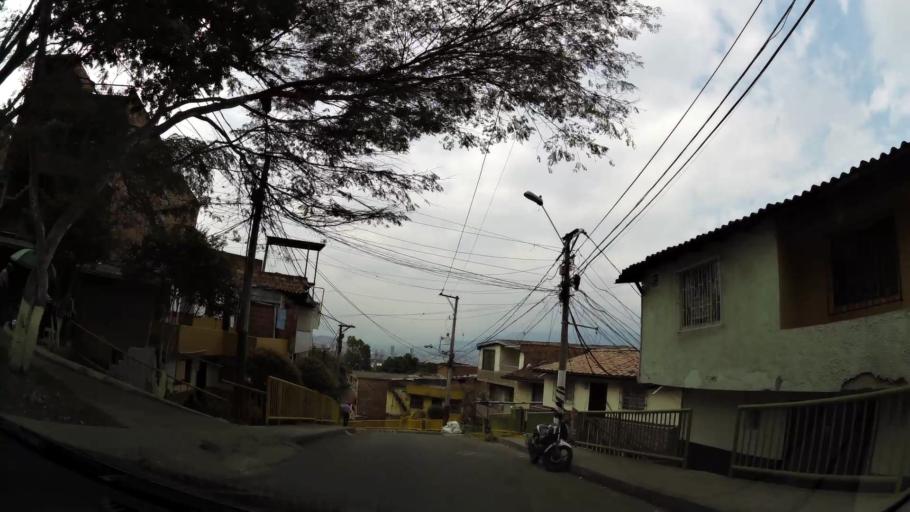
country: CO
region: Antioquia
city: Medellin
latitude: 6.2822
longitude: -75.5510
